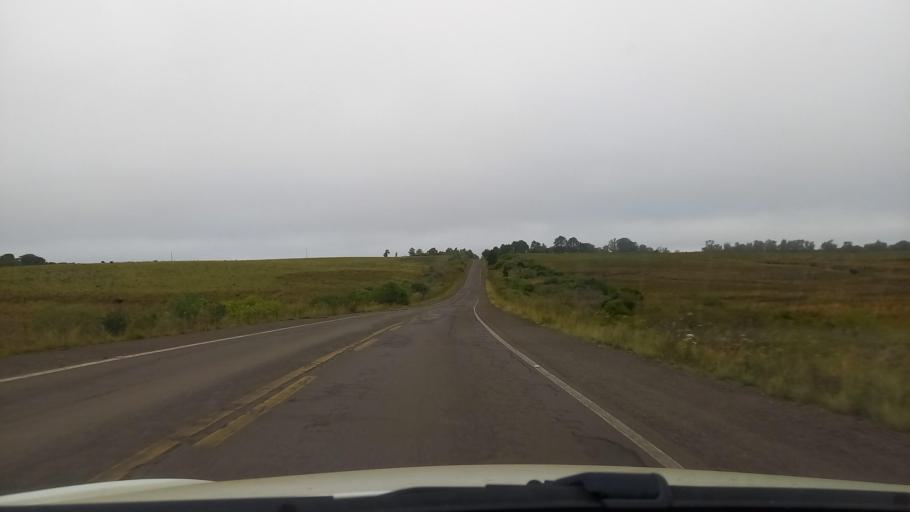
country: BR
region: Rio Grande do Sul
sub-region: Cacequi
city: Cacequi
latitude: -30.0806
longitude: -54.6187
